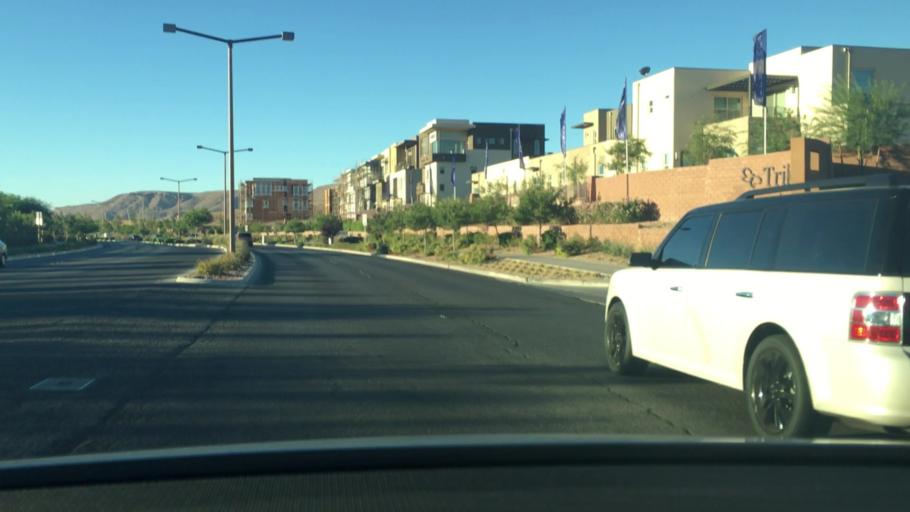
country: US
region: Nevada
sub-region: Clark County
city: Summerlin South
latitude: 36.1131
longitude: -115.3299
